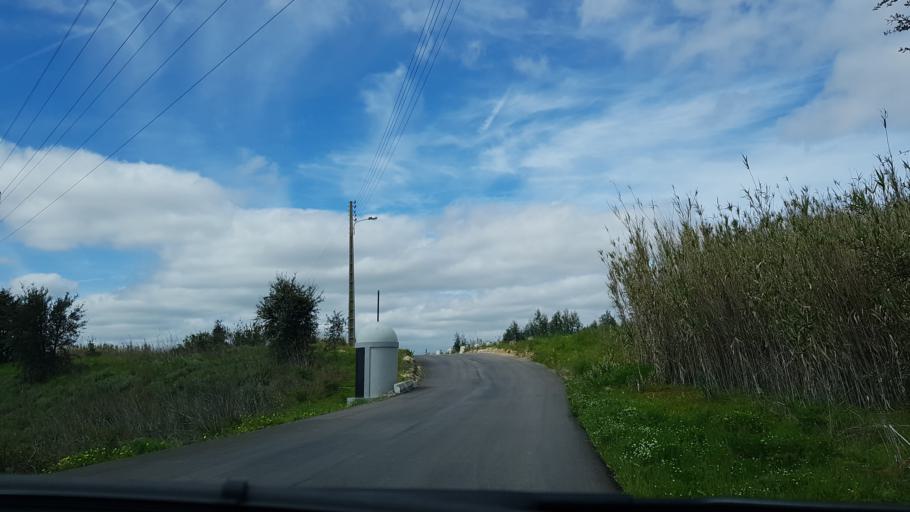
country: PT
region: Lisbon
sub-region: Alenquer
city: Carregado
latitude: 39.0447
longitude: -8.9269
